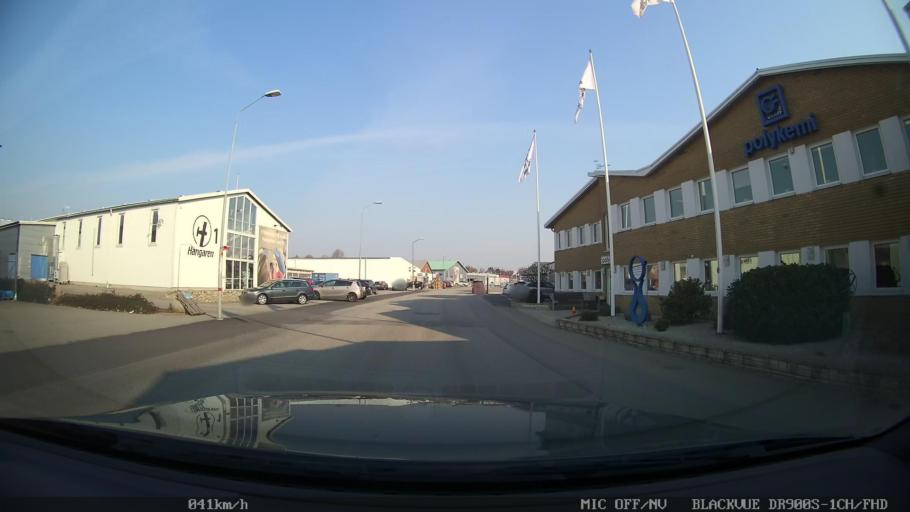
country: SE
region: Skane
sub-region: Ystads Kommun
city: Ystad
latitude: 55.4382
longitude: 13.8369
